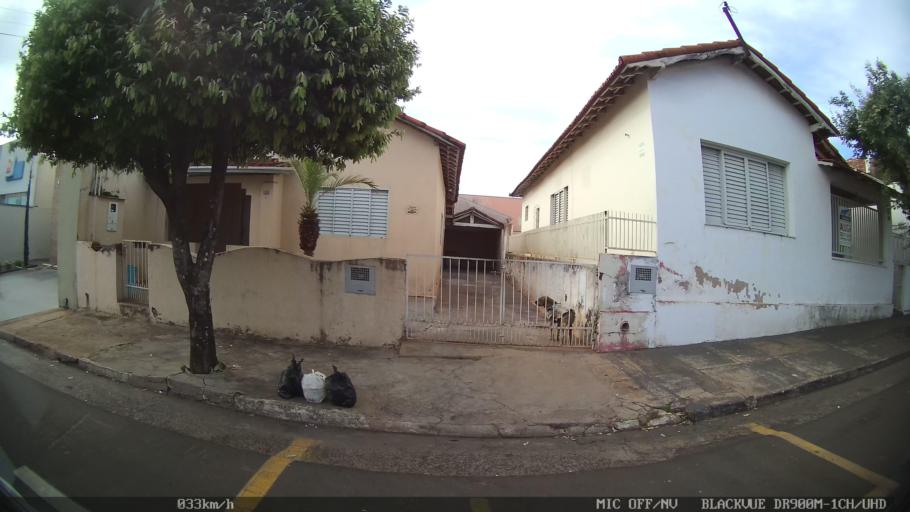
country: BR
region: Sao Paulo
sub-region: Catanduva
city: Catanduva
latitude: -21.1384
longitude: -48.9804
